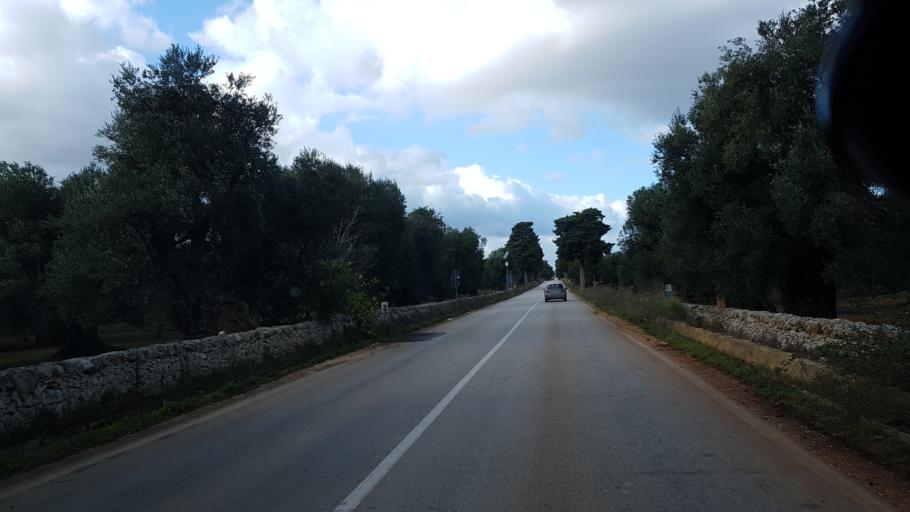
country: IT
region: Apulia
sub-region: Provincia di Brindisi
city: Montalbano
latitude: 40.7740
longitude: 17.4988
